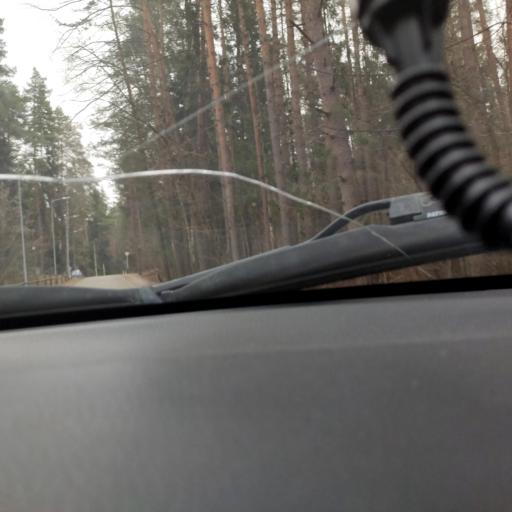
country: RU
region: Tatarstan
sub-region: Zelenodol'skiy Rayon
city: Vasil'yevo
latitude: 55.8996
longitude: 48.7359
